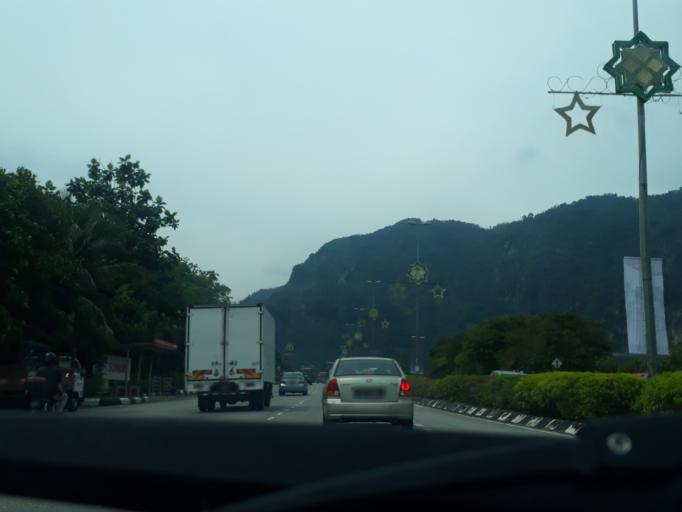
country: MY
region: Perak
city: Ipoh
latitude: 4.6224
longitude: 101.1491
